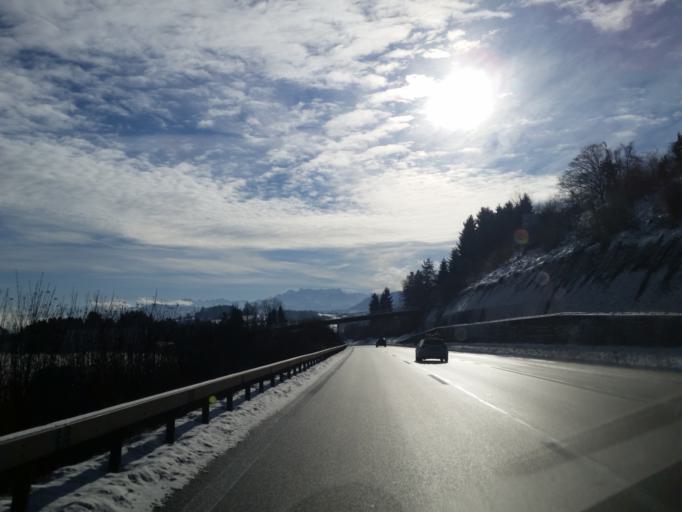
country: CH
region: Zurich
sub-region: Bezirk Horgen
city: Horgen / Allmend
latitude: 47.2364
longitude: 8.6145
